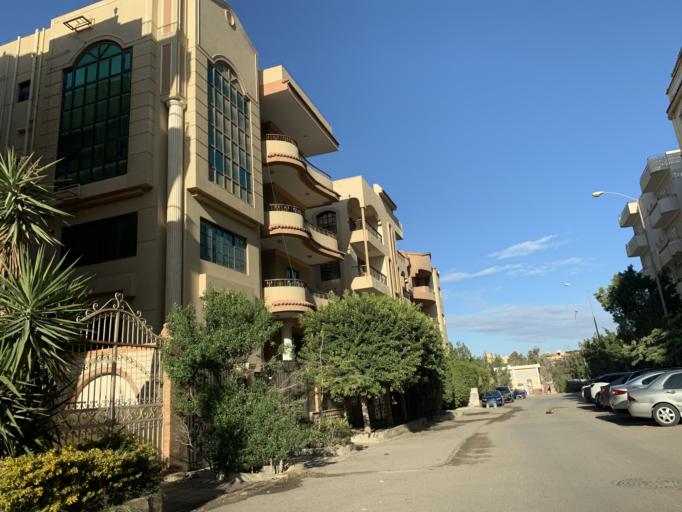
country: EG
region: Al Jizah
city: Madinat Sittah Uktubar
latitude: 29.9744
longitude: 30.9395
